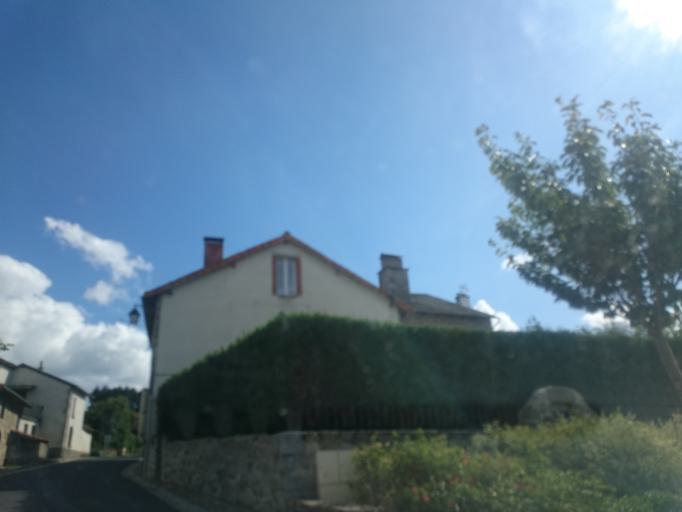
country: FR
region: Auvergne
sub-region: Departement du Cantal
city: Saint-Mamet-la-Salvetat
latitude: 44.8873
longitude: 2.2390
